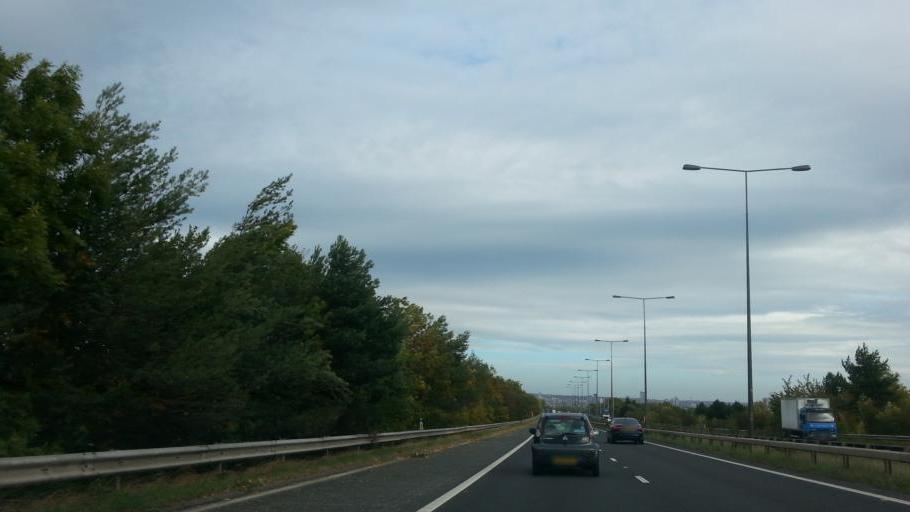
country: GB
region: England
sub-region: City and Borough of Leeds
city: Morley
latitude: 53.7650
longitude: -1.5956
